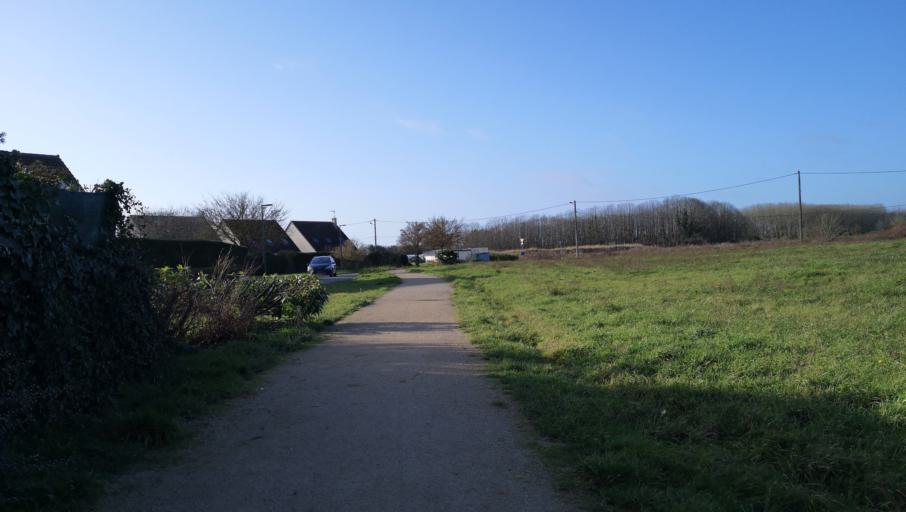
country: FR
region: Centre
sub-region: Departement du Loiret
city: Olivet
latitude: 47.8818
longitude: 1.8930
